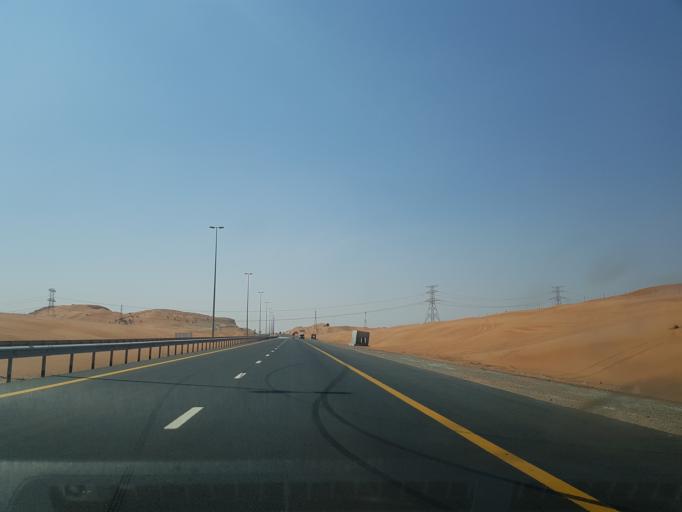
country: AE
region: Ash Shariqah
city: Adh Dhayd
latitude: 25.2458
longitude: 55.8515
